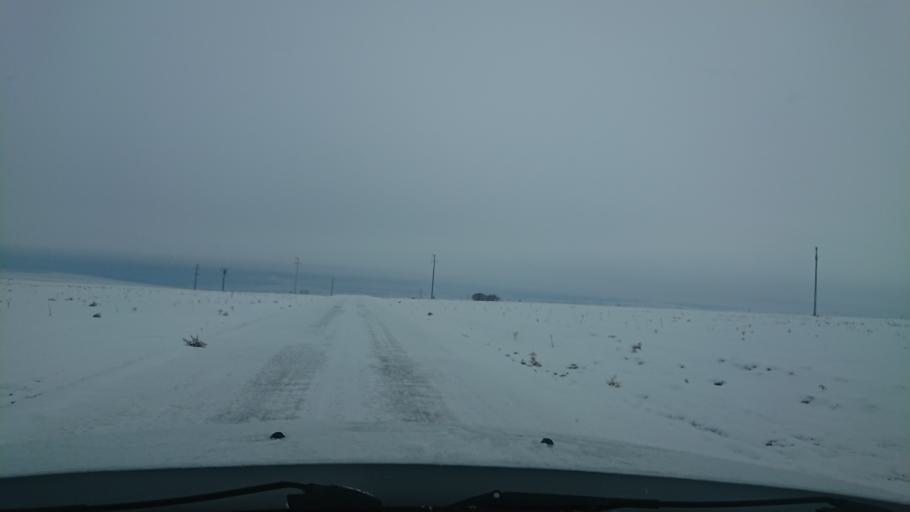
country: TR
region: Aksaray
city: Agacoren
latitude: 38.7189
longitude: 33.8673
